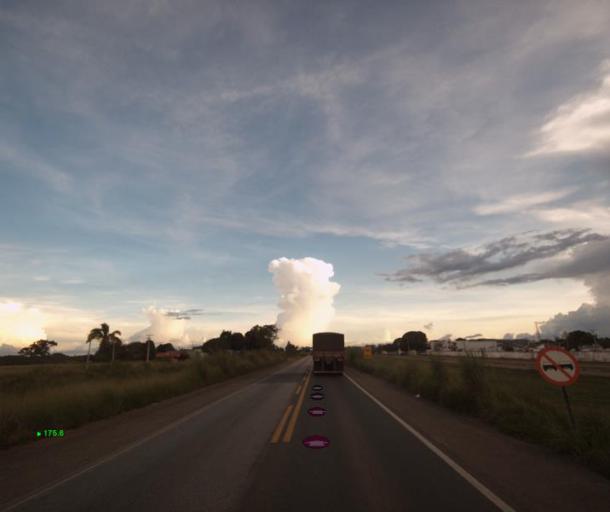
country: BR
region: Goias
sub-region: Uruacu
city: Uruacu
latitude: -14.3101
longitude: -49.1490
